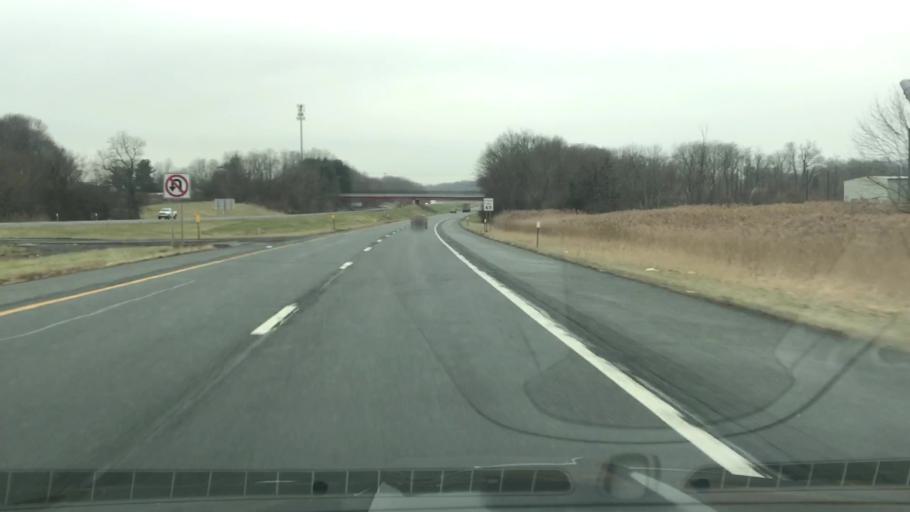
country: US
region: New York
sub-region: Orange County
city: Middletown
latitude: 41.4109
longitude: -74.4367
